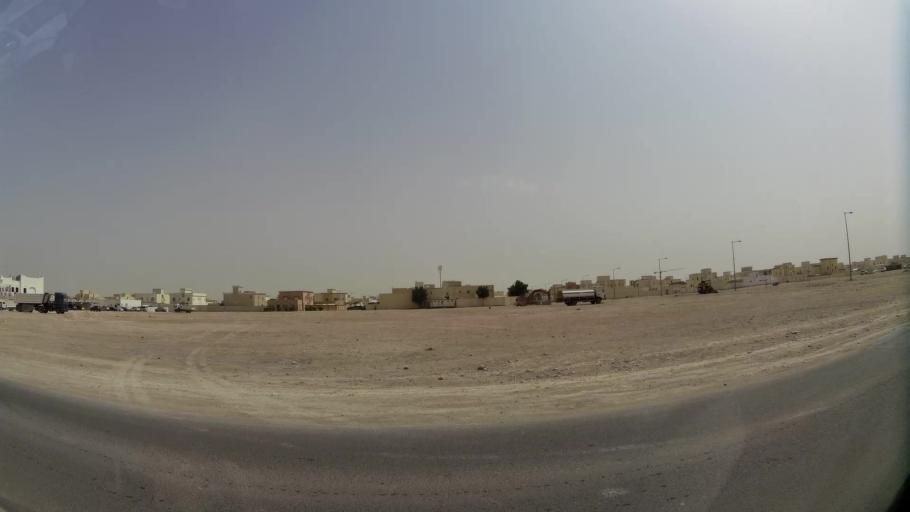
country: QA
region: Baladiyat ar Rayyan
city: Ar Rayyan
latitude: 25.2493
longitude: 51.3732
